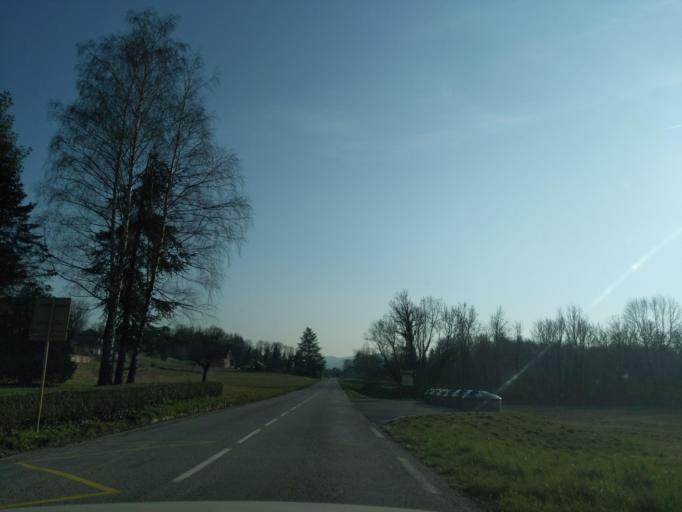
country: FR
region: Rhone-Alpes
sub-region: Departement de la Savoie
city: Chindrieux
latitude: 45.8597
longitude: 5.8420
